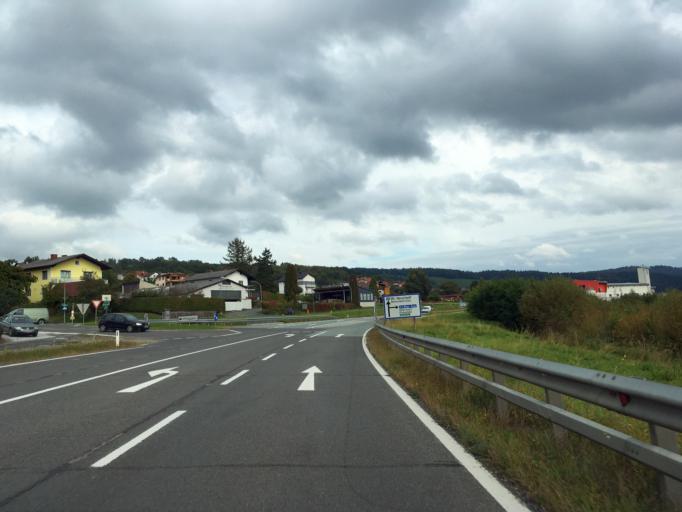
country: AT
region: Styria
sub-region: Politischer Bezirk Hartberg-Fuerstenfeld
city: Pinggau
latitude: 47.4384
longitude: 16.0702
